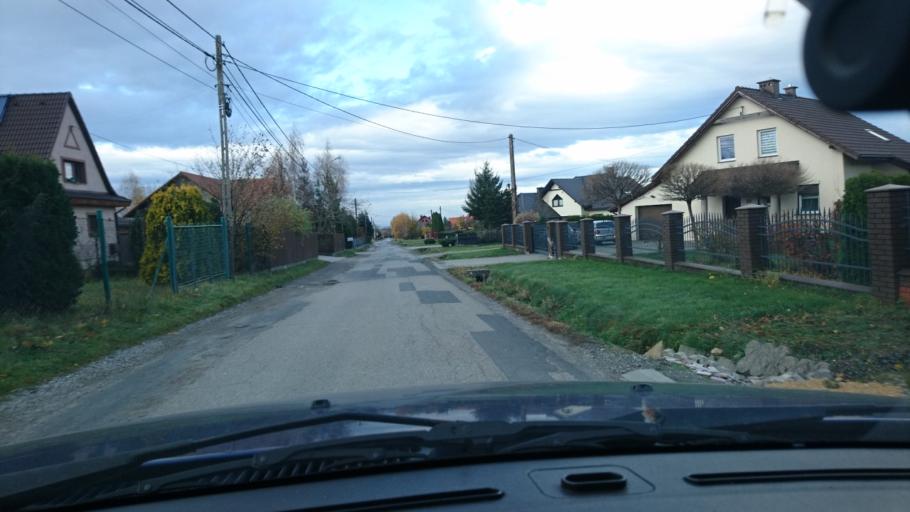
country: PL
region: Silesian Voivodeship
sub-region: Powiat bielski
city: Kozy
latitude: 49.8309
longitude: 19.1187
